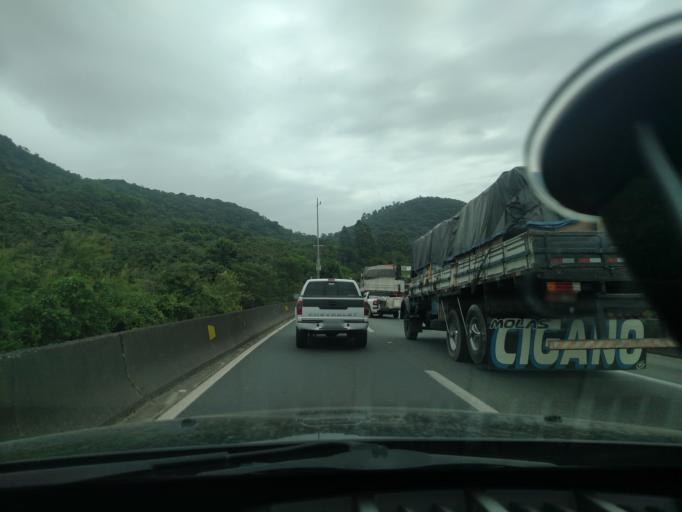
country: BR
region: Santa Catarina
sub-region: Itapema
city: Itapema
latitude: -27.0557
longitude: -48.5986
